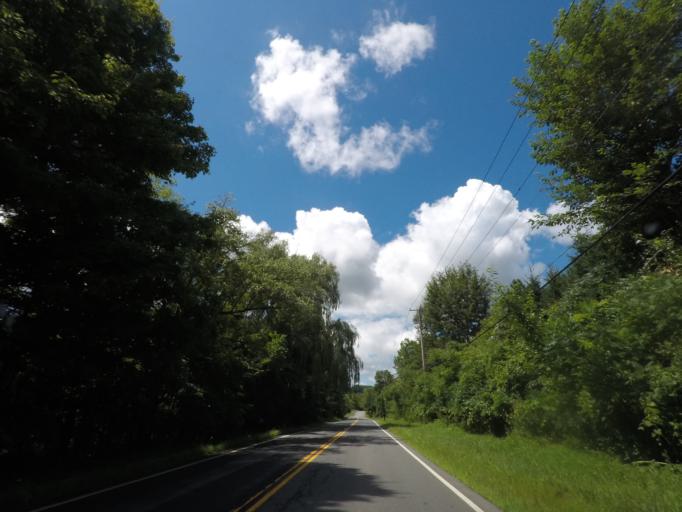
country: US
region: New York
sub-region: Rensselaer County
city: Wynantskill
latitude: 42.6675
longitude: -73.6552
